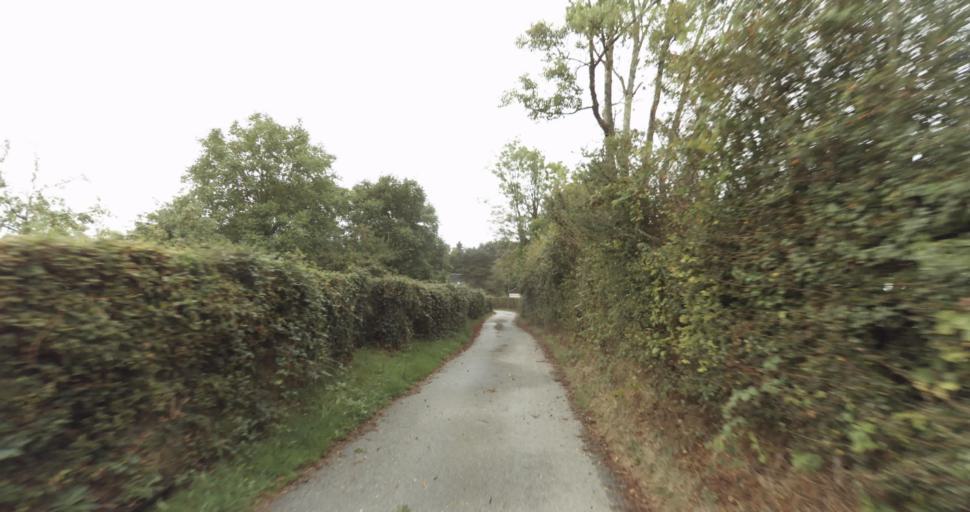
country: FR
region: Lower Normandy
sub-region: Departement de l'Orne
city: Sainte-Gauburge-Sainte-Colombe
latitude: 48.7490
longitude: 0.4200
